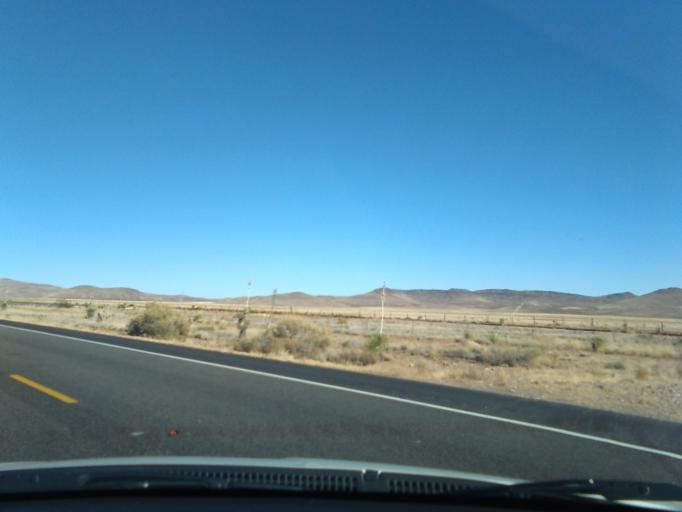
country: US
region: New Mexico
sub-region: Luna County
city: Deming
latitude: 32.4945
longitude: -107.5173
